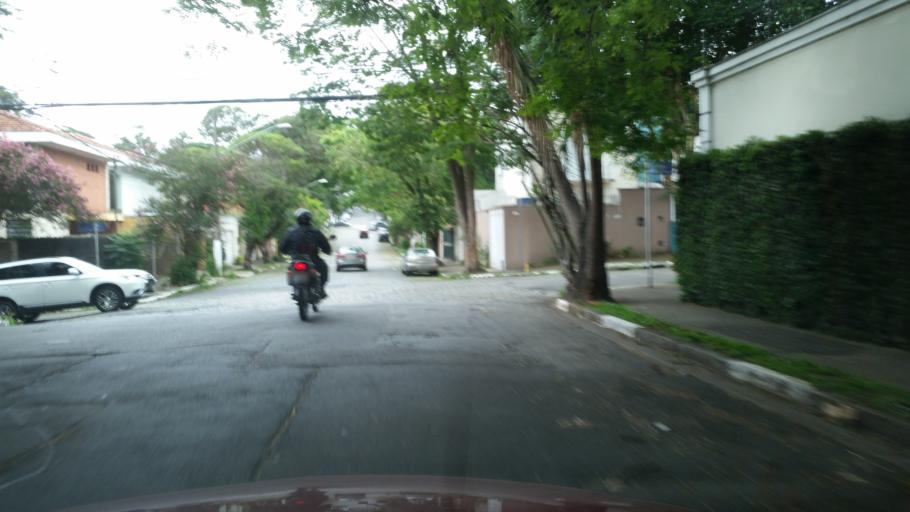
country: BR
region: Sao Paulo
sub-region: Diadema
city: Diadema
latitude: -23.6457
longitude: -46.6982
